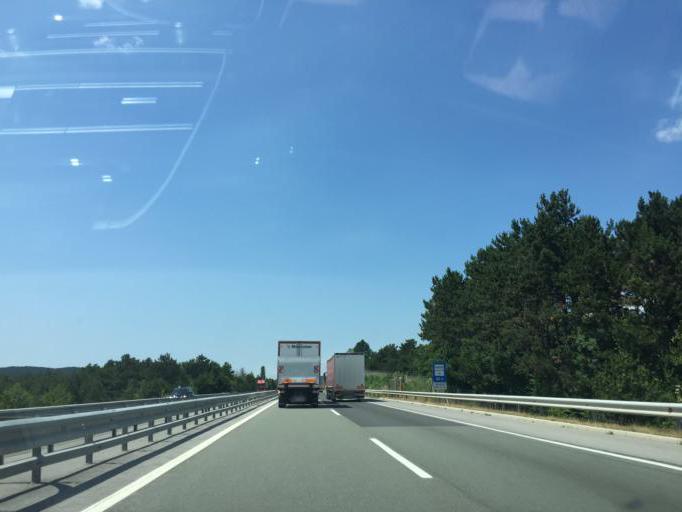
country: SI
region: Divaca
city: Divaca
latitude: 45.6975
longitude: 13.9596
